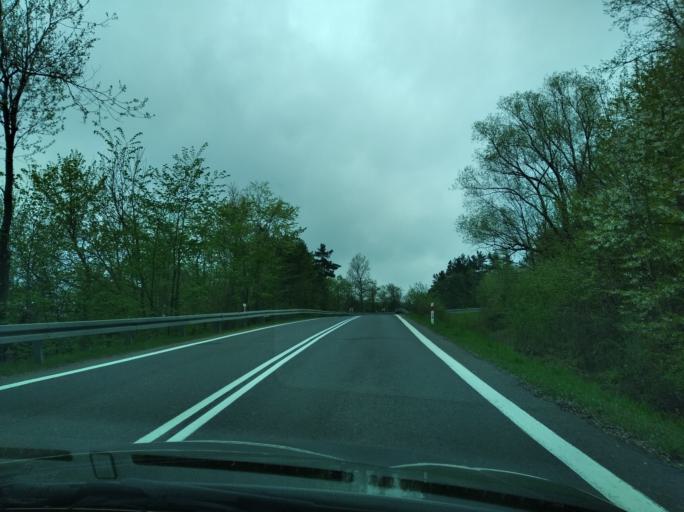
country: PL
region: Subcarpathian Voivodeship
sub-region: Powiat sanocki
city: Tyrawa Woloska
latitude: 49.5533
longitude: 22.3207
